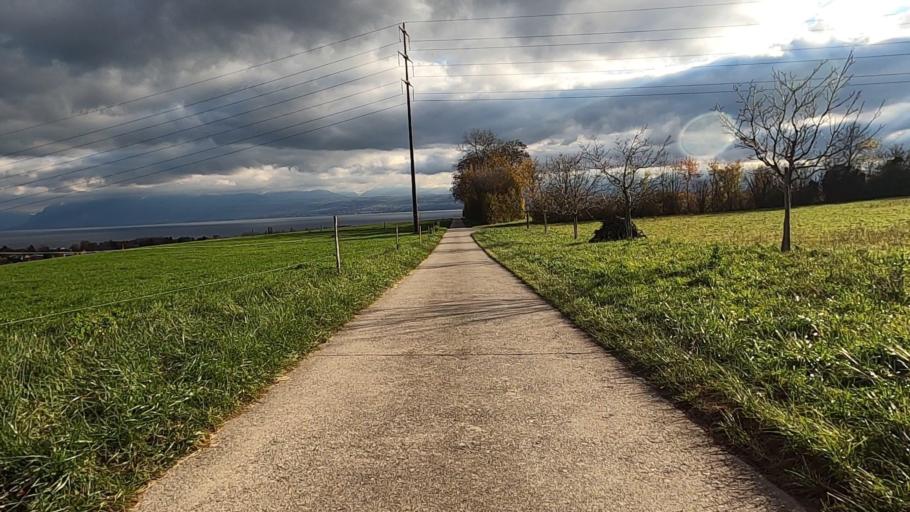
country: CH
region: Vaud
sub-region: Morges District
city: Saint-Prex
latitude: 46.5114
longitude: 6.4569
